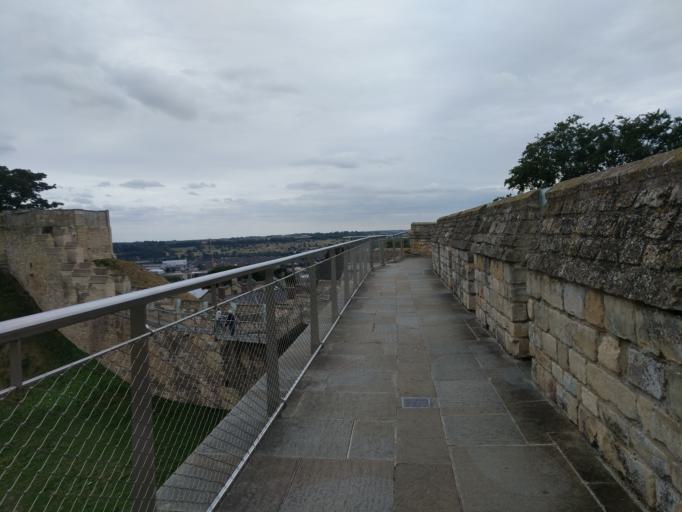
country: GB
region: England
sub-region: Lincolnshire
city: Lincoln
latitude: 53.2348
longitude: -0.5424
